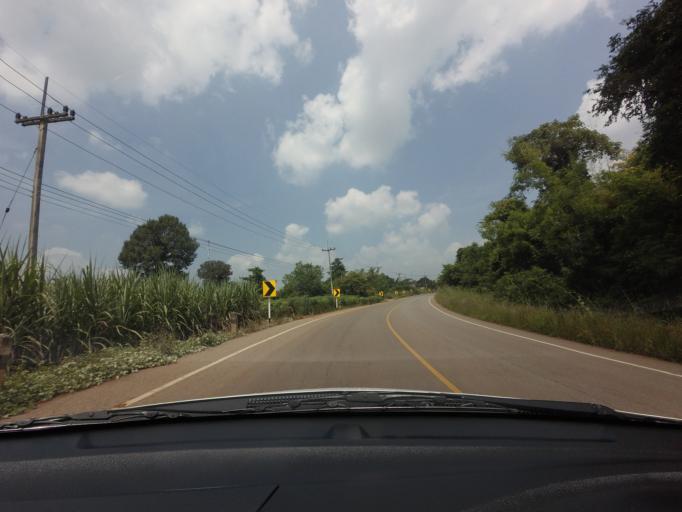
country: TH
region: Nakhon Ratchasima
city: Pak Chong
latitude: 14.5815
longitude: 101.5658
